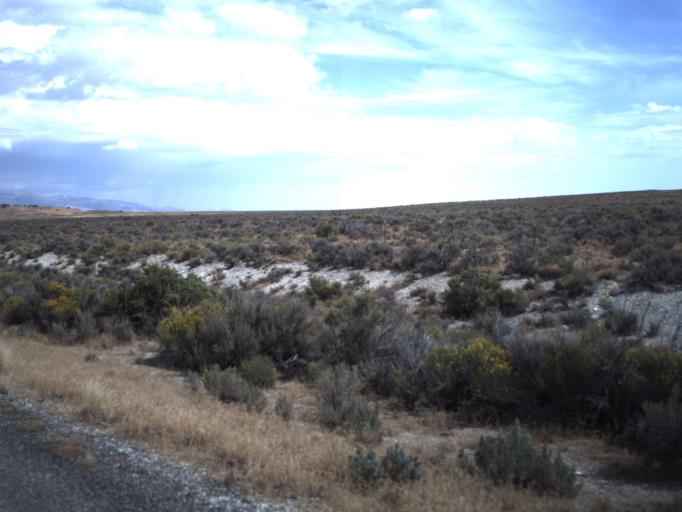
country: US
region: Idaho
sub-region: Cassia County
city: Burley
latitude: 41.6648
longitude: -113.5463
